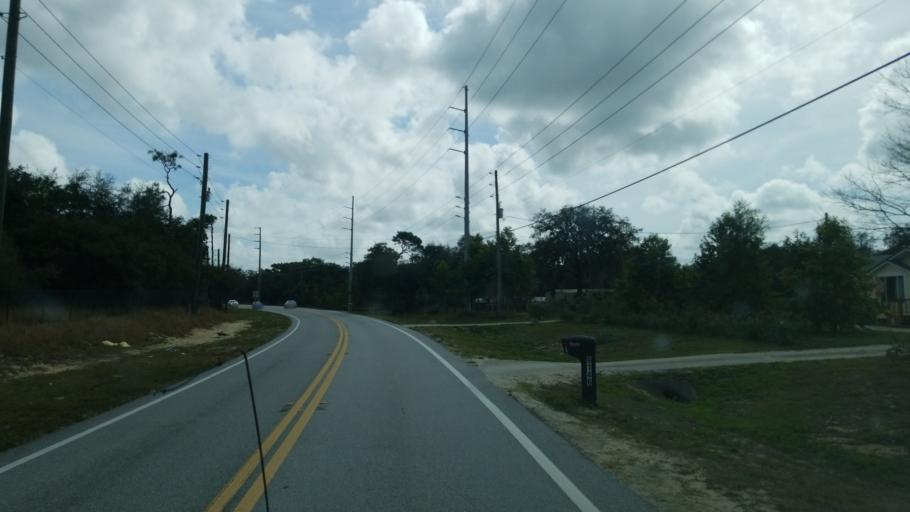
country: US
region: Florida
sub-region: Polk County
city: Dundee
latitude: 28.0277
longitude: -81.5156
